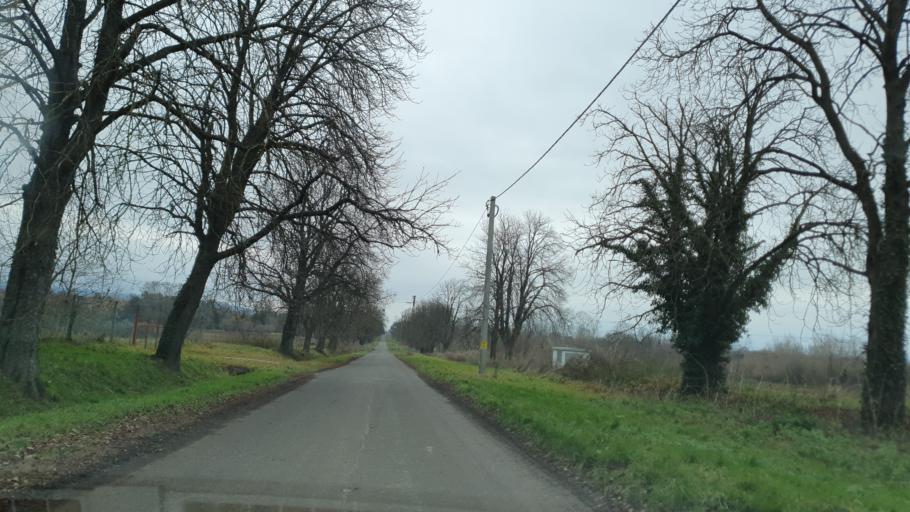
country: HU
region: Zala
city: Keszthely
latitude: 46.7489
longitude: 17.2303
